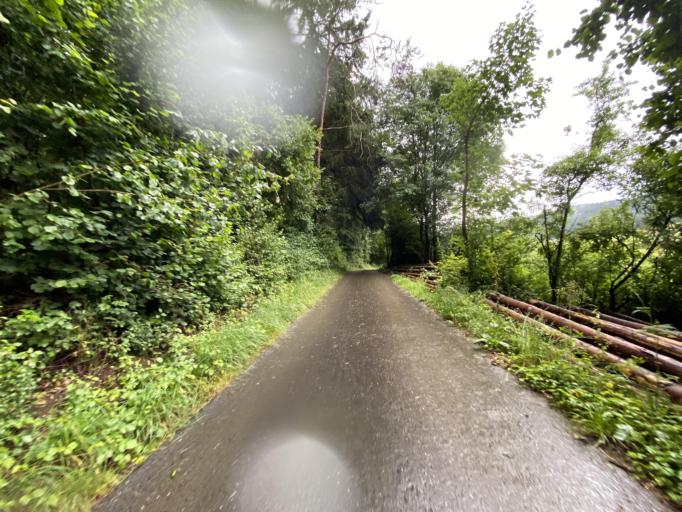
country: DE
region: Baden-Wuerttemberg
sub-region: Tuebingen Region
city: Sigmaringen
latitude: 48.1219
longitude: 9.2168
